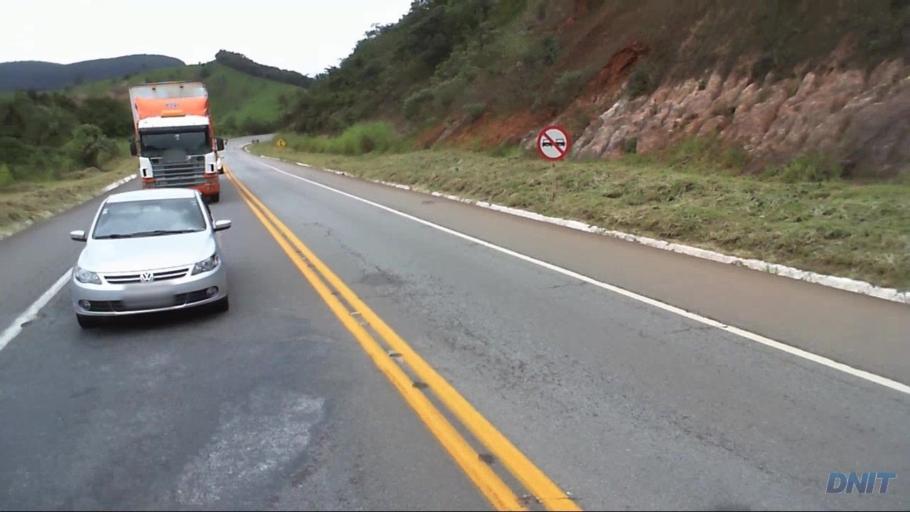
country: BR
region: Minas Gerais
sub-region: Joao Monlevade
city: Joao Monlevade
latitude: -19.8481
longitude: -43.2516
